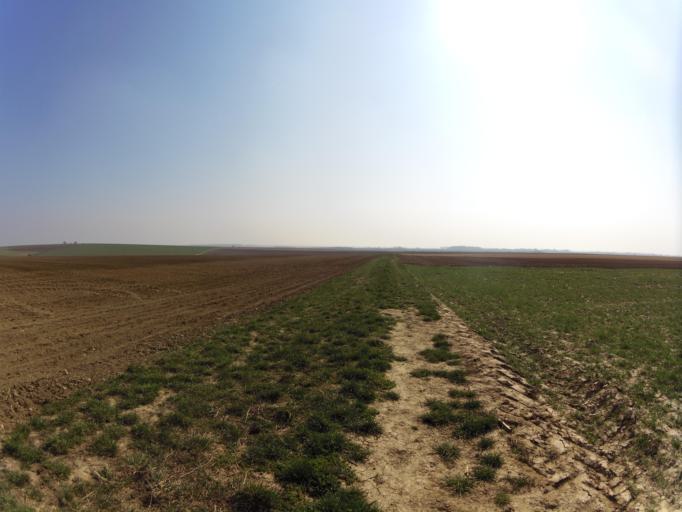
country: DE
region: Bavaria
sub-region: Regierungsbezirk Unterfranken
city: Eibelstadt
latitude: 49.6891
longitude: 9.9797
